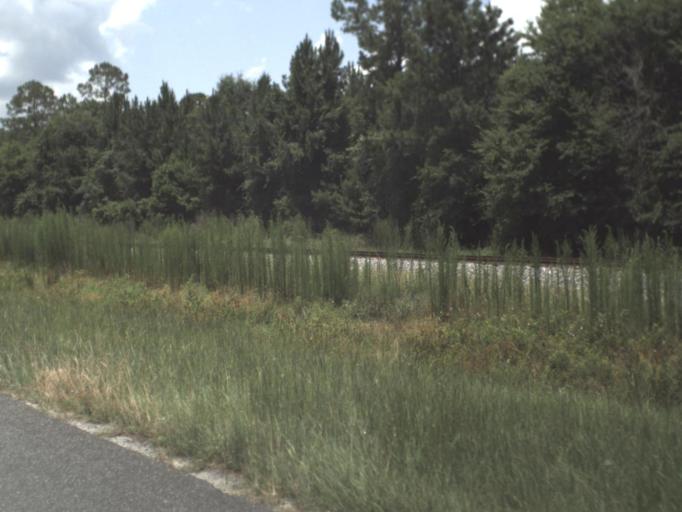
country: US
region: Florida
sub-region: Columbia County
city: Five Points
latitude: 30.2631
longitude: -82.6872
